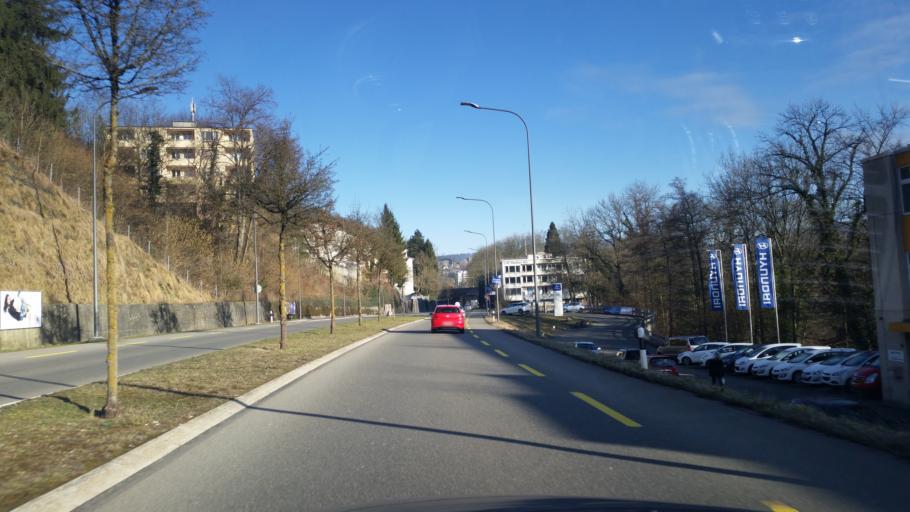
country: CH
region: Aargau
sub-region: Bezirk Baden
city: Baden
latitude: 47.4616
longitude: 8.3078
